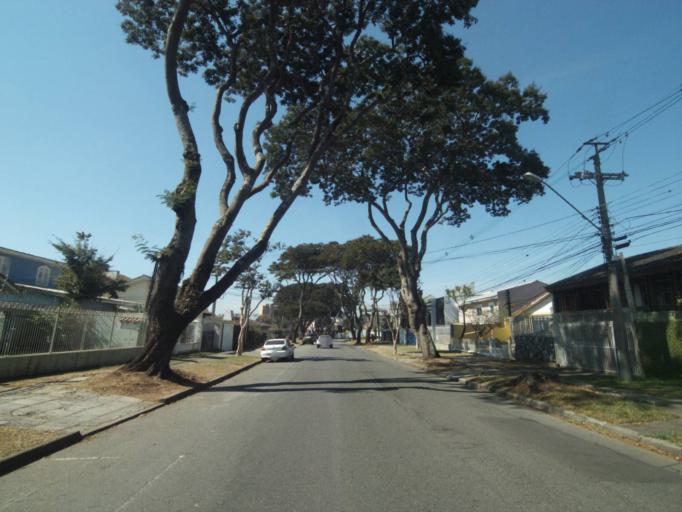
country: BR
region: Parana
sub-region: Curitiba
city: Curitiba
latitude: -25.4550
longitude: -49.2740
